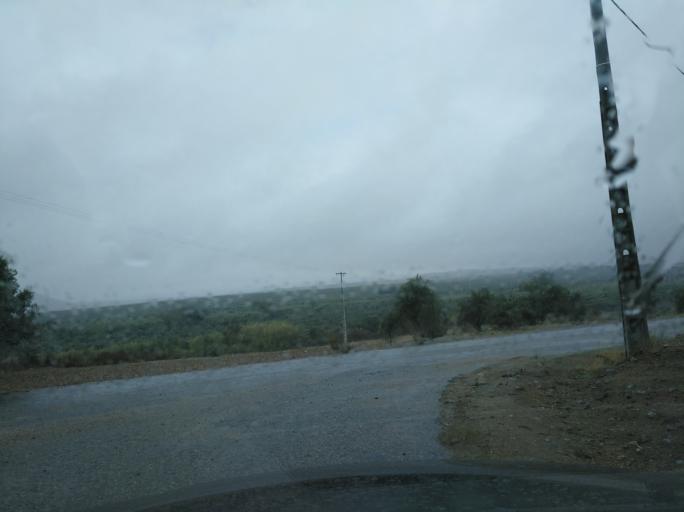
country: PT
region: Portalegre
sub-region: Campo Maior
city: Campo Maior
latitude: 38.9651
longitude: -7.0723
